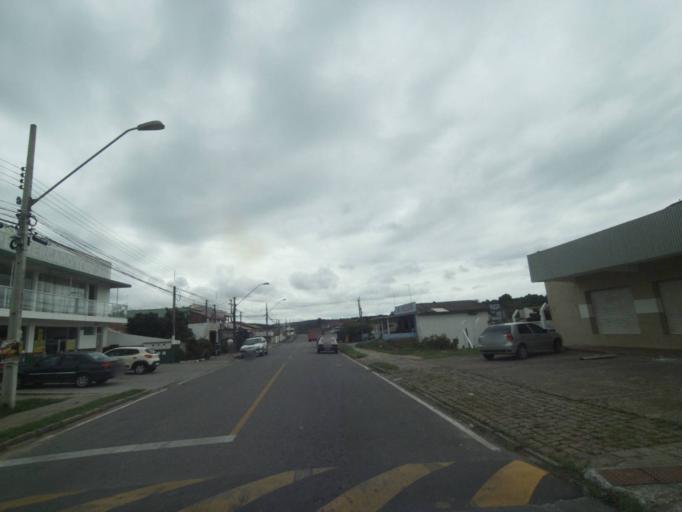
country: BR
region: Parana
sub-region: Quatro Barras
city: Quatro Barras
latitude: -25.3507
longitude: -49.1104
